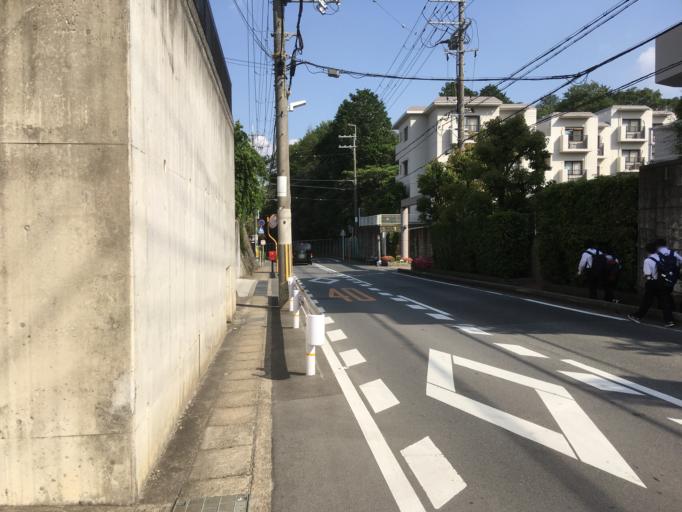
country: JP
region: Nara
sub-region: Ikoma-shi
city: Ikoma
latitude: 34.6843
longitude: 135.7026
